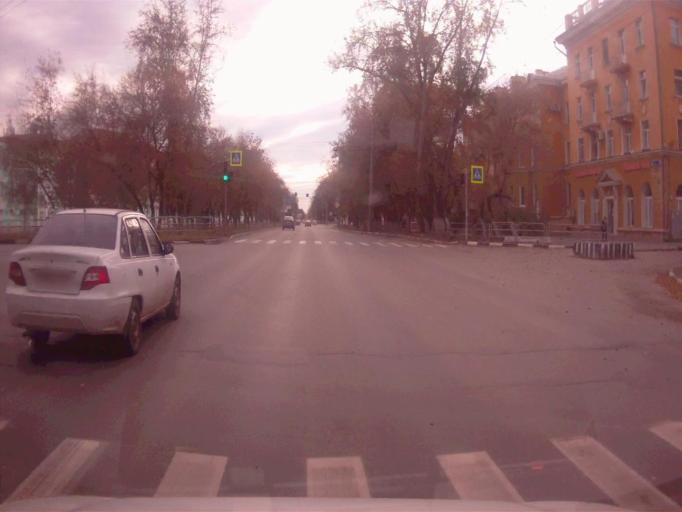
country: RU
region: Chelyabinsk
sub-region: Gorod Chelyabinsk
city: Chelyabinsk
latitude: 55.1228
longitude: 61.4737
